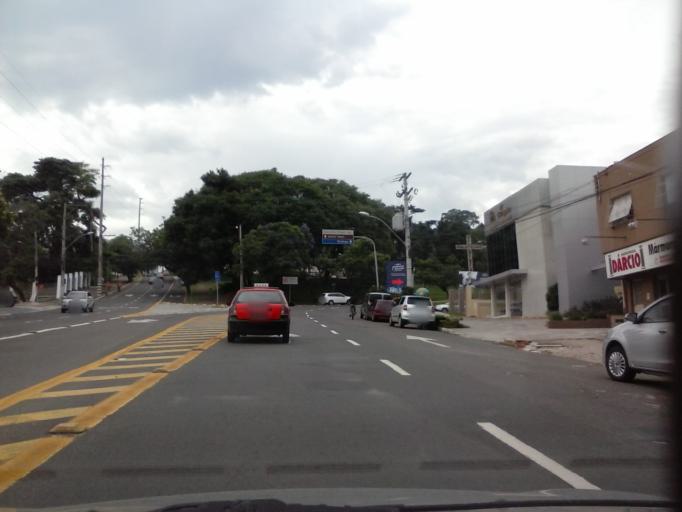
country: BR
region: Rio Grande do Sul
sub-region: Porto Alegre
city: Porto Alegre
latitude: -30.0530
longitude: -51.2122
